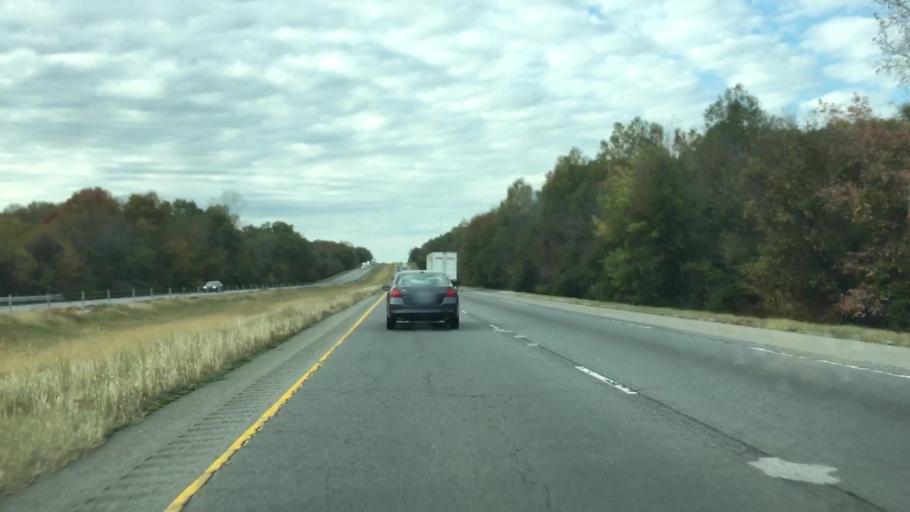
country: US
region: Arkansas
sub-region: Faulkner County
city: Conway
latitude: 35.1398
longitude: -92.5251
